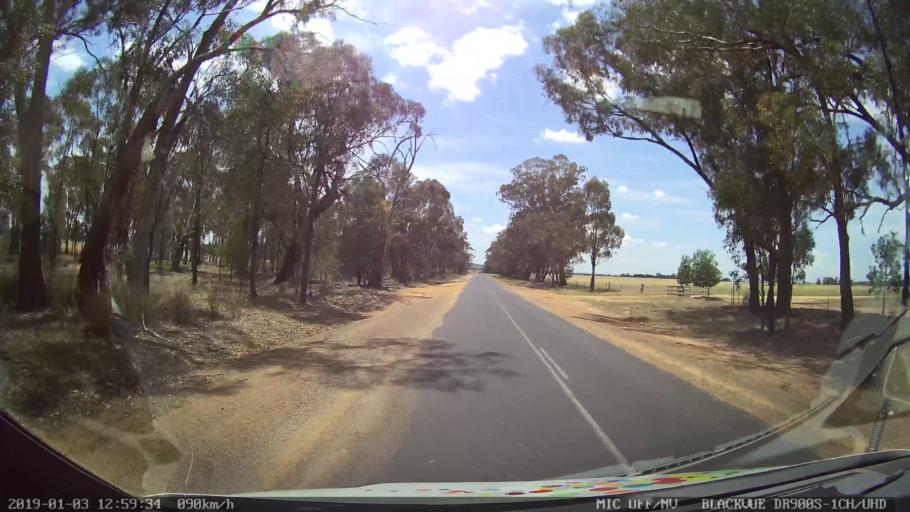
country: AU
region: New South Wales
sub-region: Cabonne
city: Canowindra
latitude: -33.6359
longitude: 148.3910
